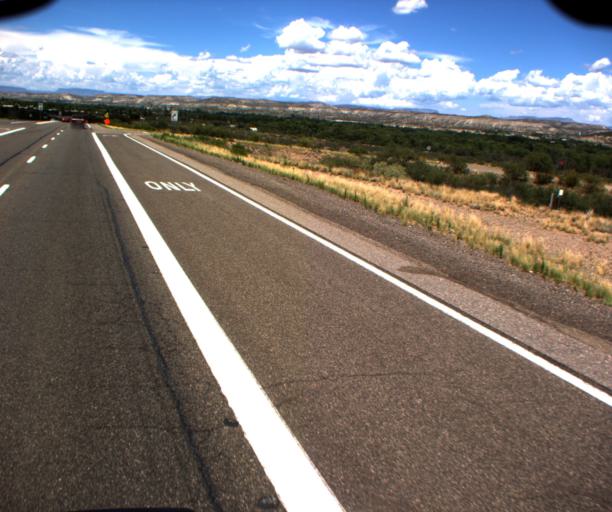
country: US
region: Arizona
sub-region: Yavapai County
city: Camp Verde
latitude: 34.5834
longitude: -111.8862
